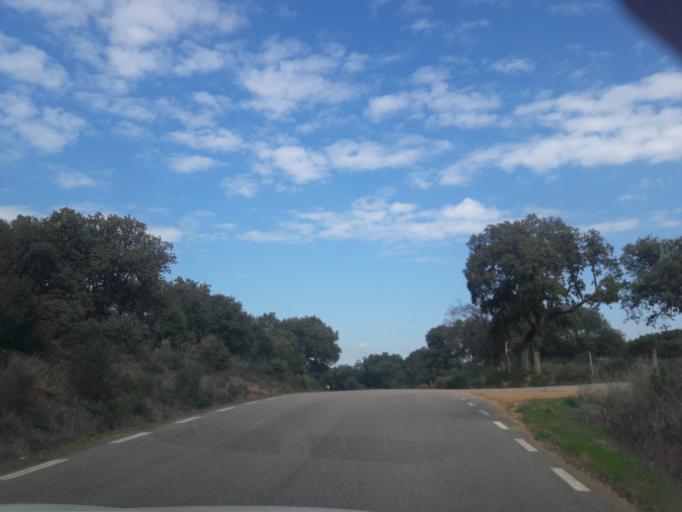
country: ES
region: Castille and Leon
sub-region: Provincia de Salamanca
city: Zamarra
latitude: 40.5581
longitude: -6.4532
